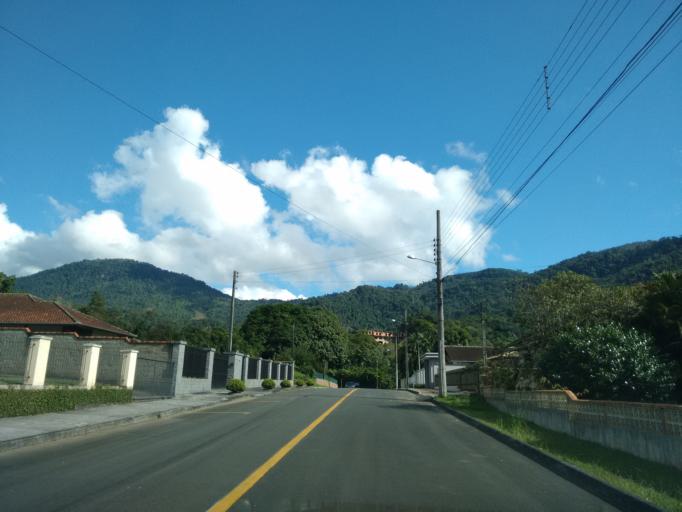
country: BR
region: Santa Catarina
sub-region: Pomerode
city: Pomerode
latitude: -26.7486
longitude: -49.1768
